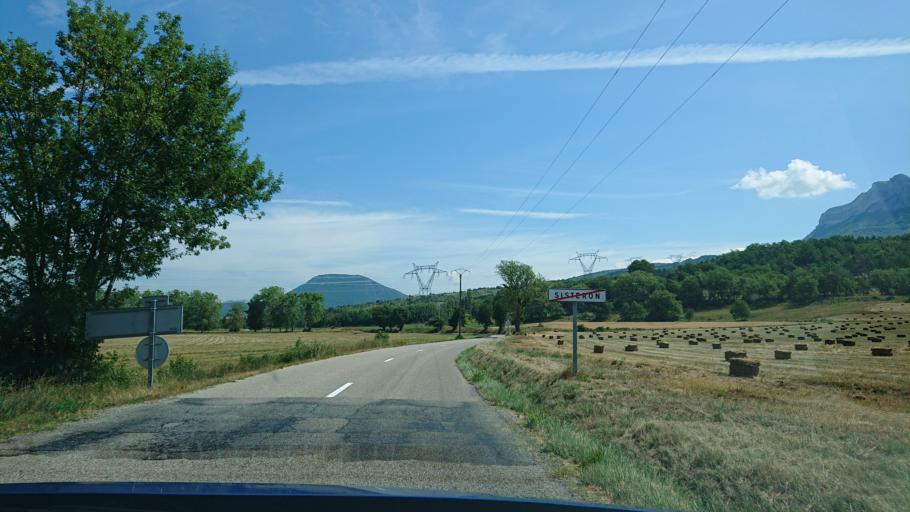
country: FR
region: Provence-Alpes-Cote d'Azur
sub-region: Departement des Alpes-de-Haute-Provence
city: Sisteron
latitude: 44.2269
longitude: 5.9407
